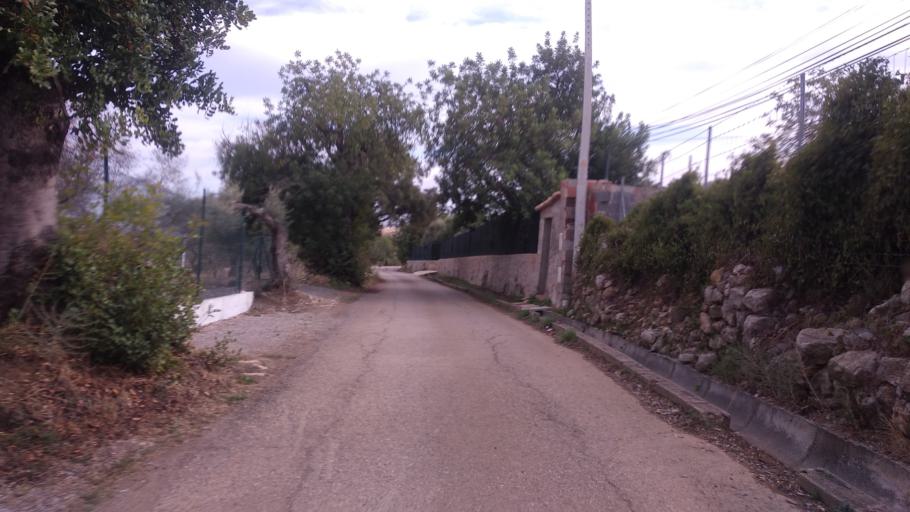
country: PT
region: Faro
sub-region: Sao Bras de Alportel
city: Sao Bras de Alportel
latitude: 37.1561
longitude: -7.8980
